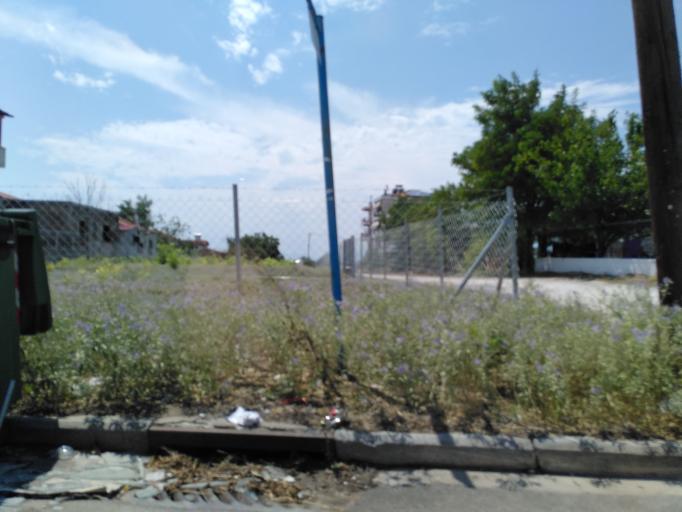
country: GR
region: Central Macedonia
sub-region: Nomos Thessalonikis
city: Epanomi
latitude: 40.4304
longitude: 22.9222
